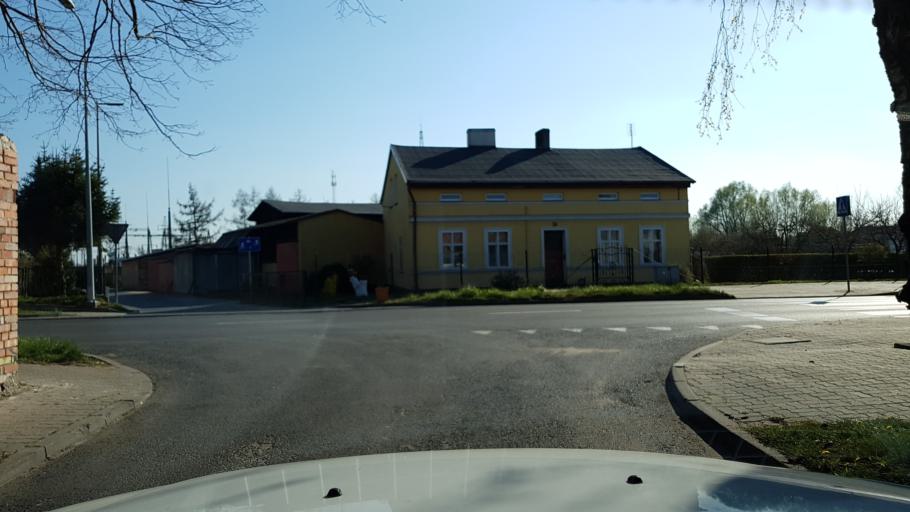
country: PL
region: West Pomeranian Voivodeship
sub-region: Powiat slawienski
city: Darlowo
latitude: 54.4143
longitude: 16.4146
